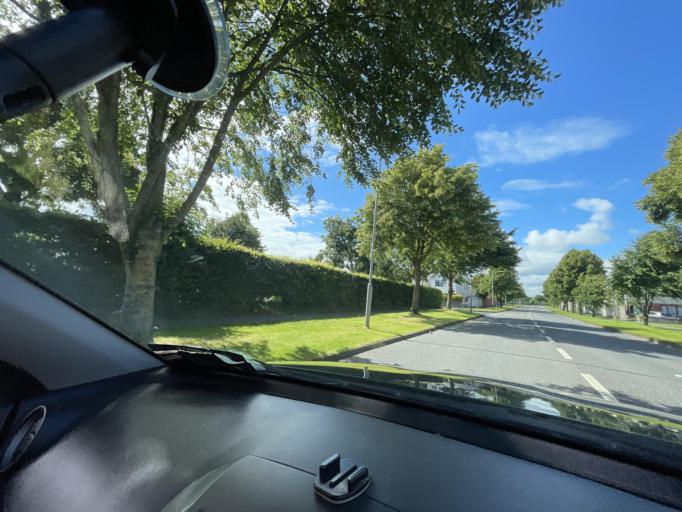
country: IE
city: Cherry Orchard
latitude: 53.3249
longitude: -6.3810
